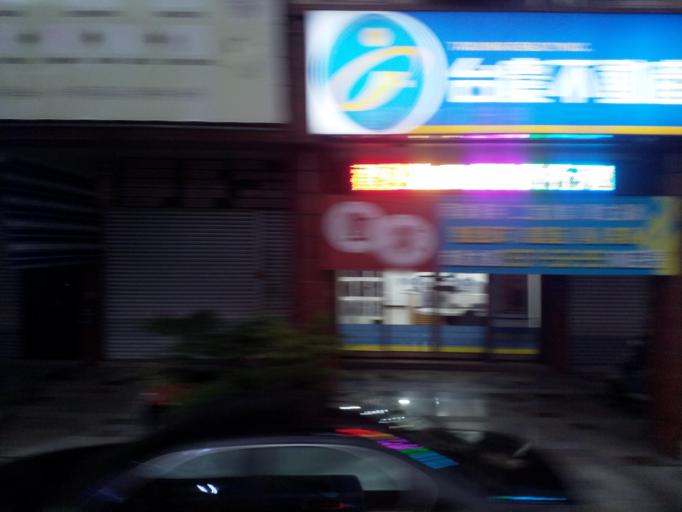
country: TW
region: Kaohsiung
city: Kaohsiung
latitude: 22.6868
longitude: 120.3103
